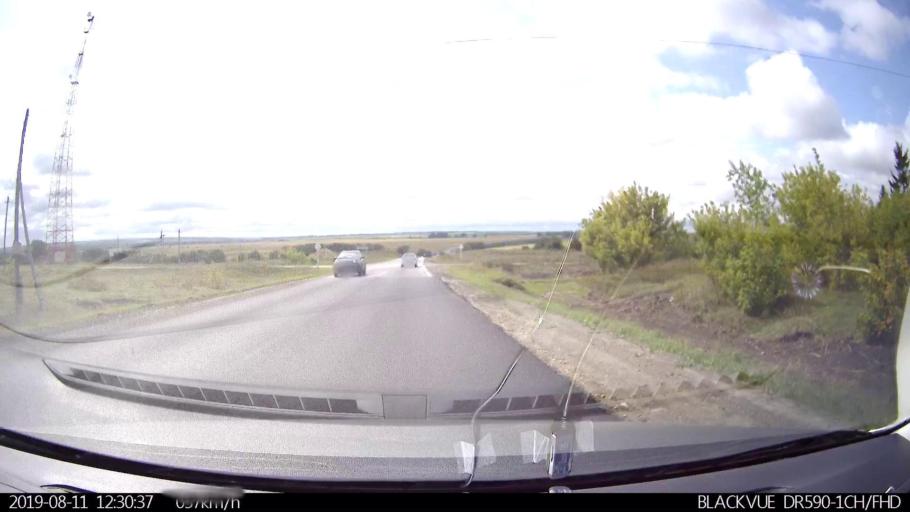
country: RU
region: Ulyanovsk
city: Ignatovka
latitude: 53.8244
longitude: 47.8922
